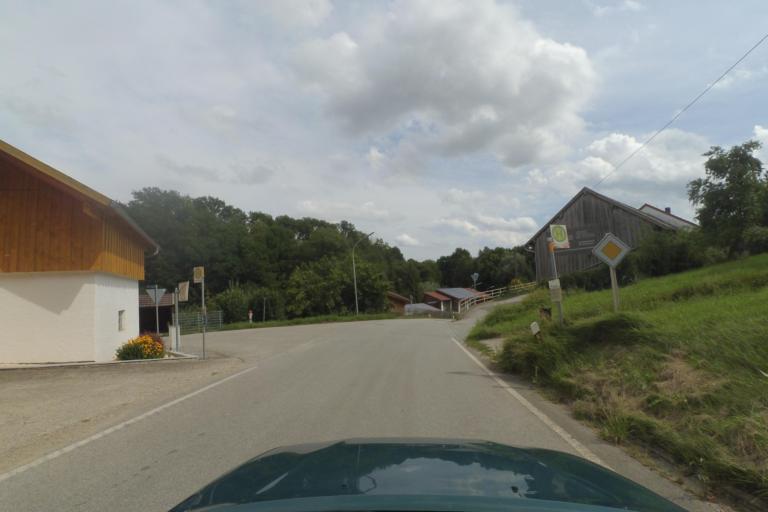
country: DE
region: Bavaria
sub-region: Lower Bavaria
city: Oberporing
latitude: 48.6864
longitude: 12.7724
